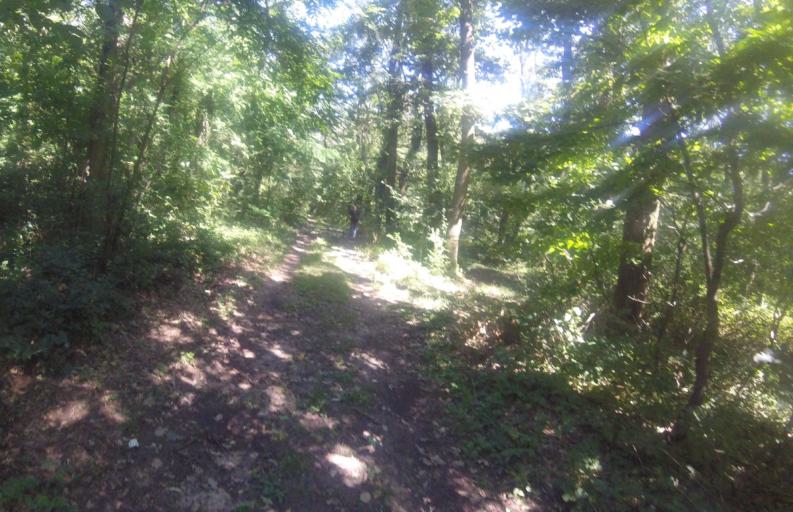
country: HU
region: Zala
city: Heviz
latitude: 46.8138
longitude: 17.1842
